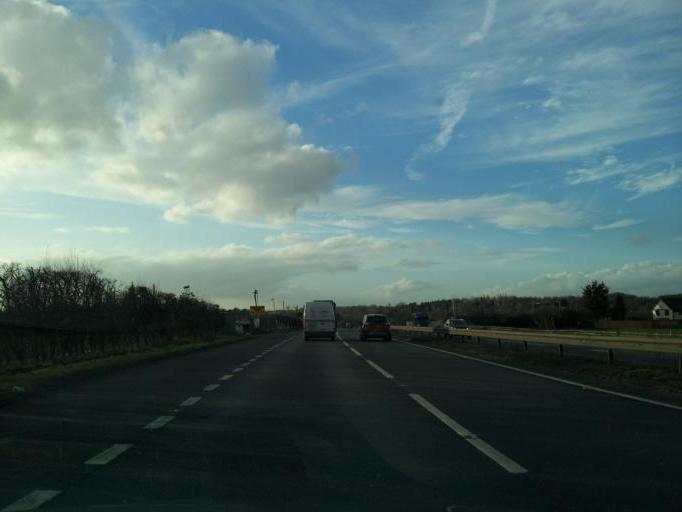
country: GB
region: England
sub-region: Peterborough
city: Wansford
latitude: 52.5758
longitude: -0.4057
